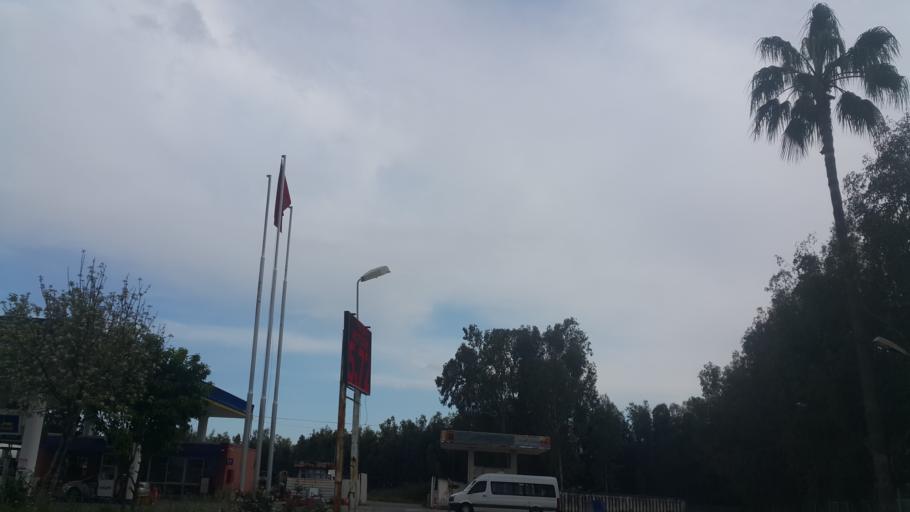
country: TR
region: Mersin
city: Yenice
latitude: 36.9776
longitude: 35.0774
